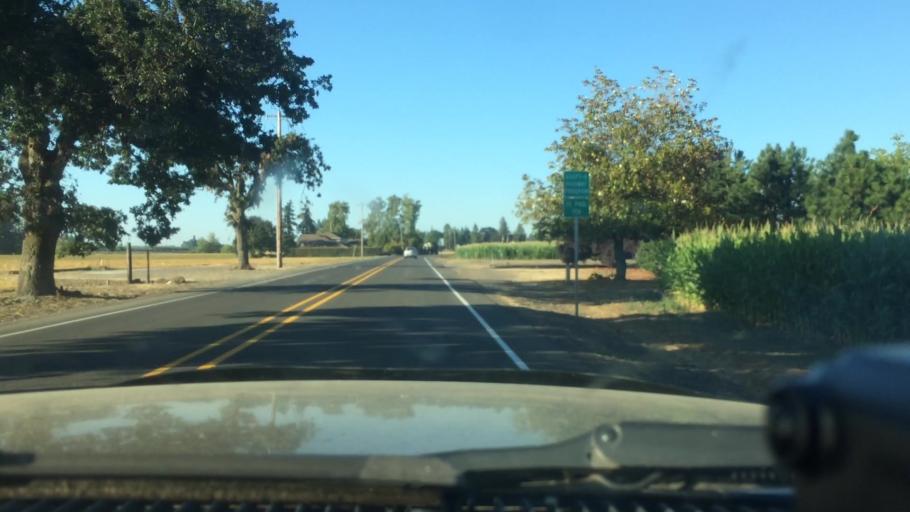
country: US
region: Oregon
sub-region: Yamhill County
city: Dundee
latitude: 45.2214
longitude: -122.9702
